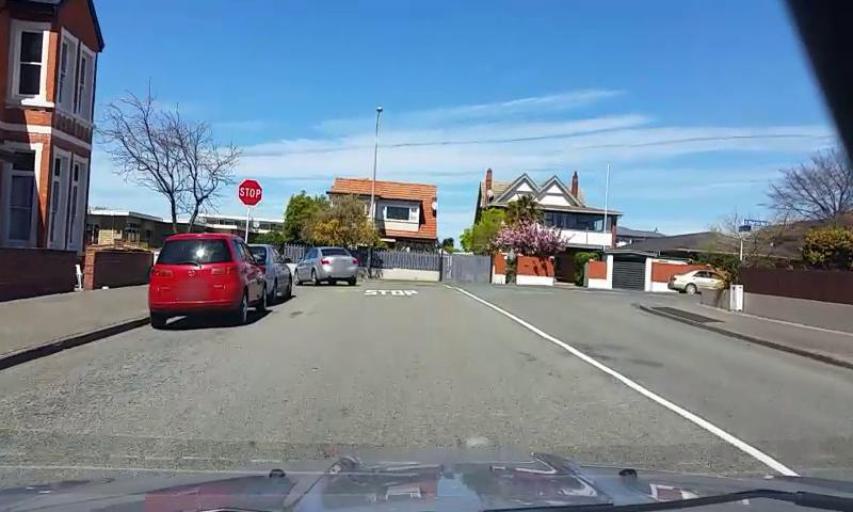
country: NZ
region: Canterbury
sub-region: Timaru District
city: Timaru
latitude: -44.3905
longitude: 171.2406
